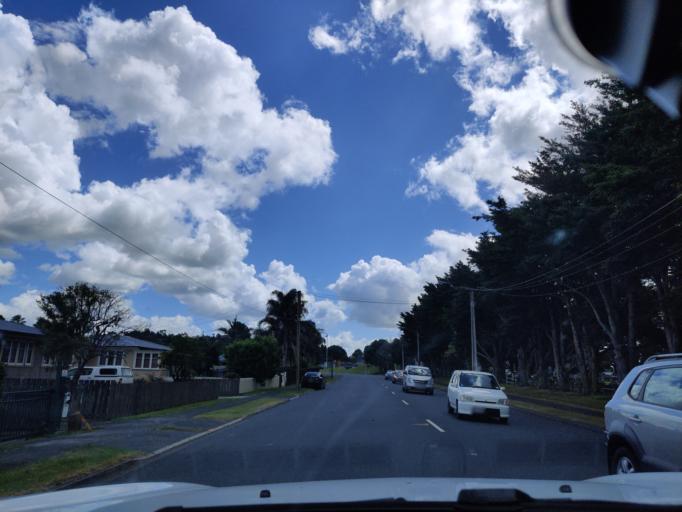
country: NZ
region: Auckland
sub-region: Auckland
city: Papakura
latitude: -37.0703
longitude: 174.9452
